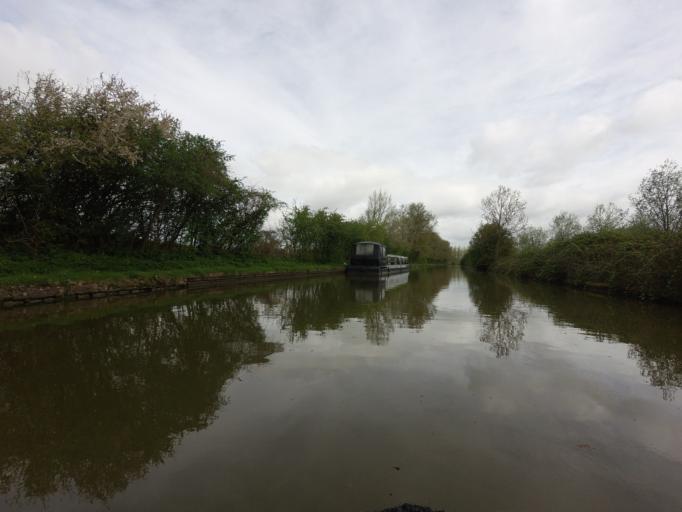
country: GB
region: England
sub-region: Milton Keynes
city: Water Eaton
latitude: 51.9505
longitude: -0.7081
